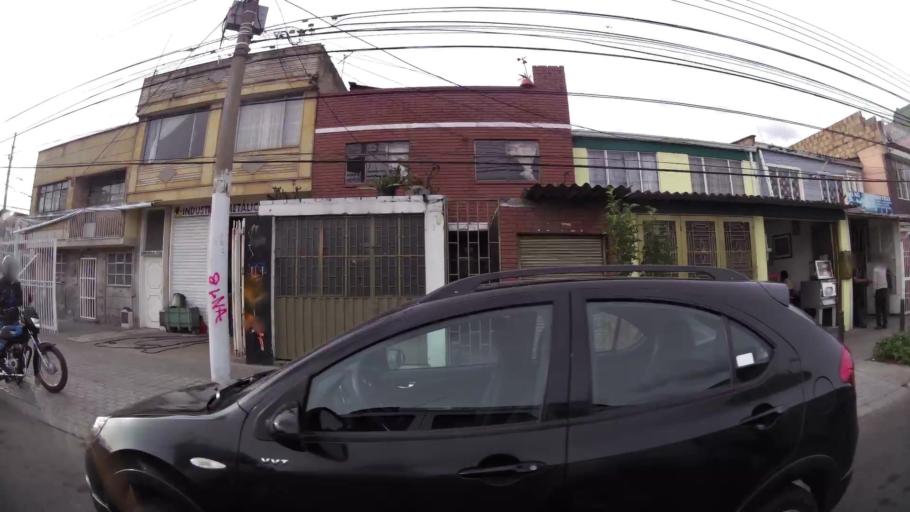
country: CO
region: Cundinamarca
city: Soacha
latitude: 4.6197
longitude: -74.1576
